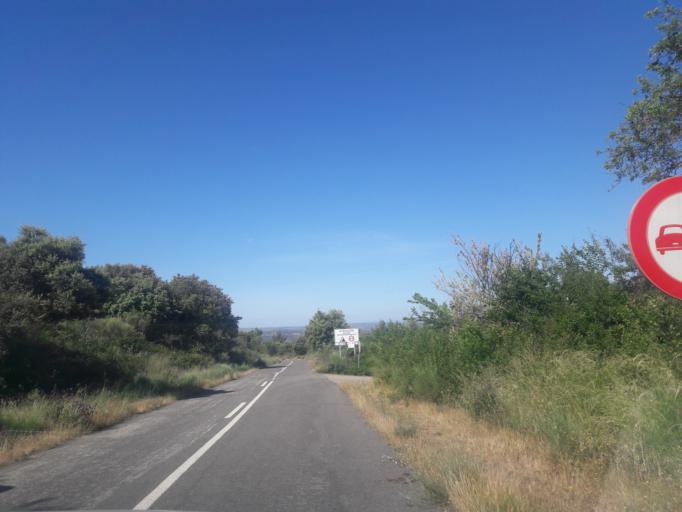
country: ES
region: Castille and Leon
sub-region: Provincia de Salamanca
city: Saucelle
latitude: 41.0367
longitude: -6.7659
